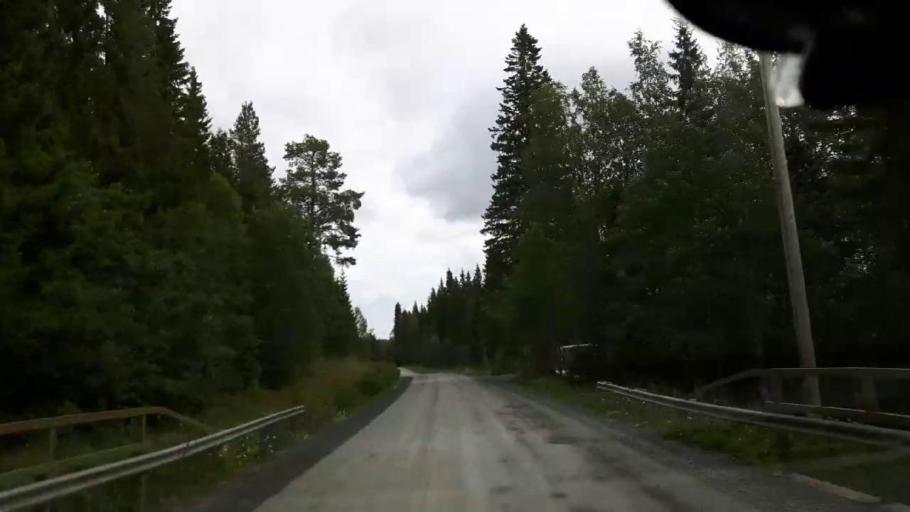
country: SE
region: Jaemtland
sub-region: Krokoms Kommun
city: Valla
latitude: 63.6151
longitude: 14.0897
